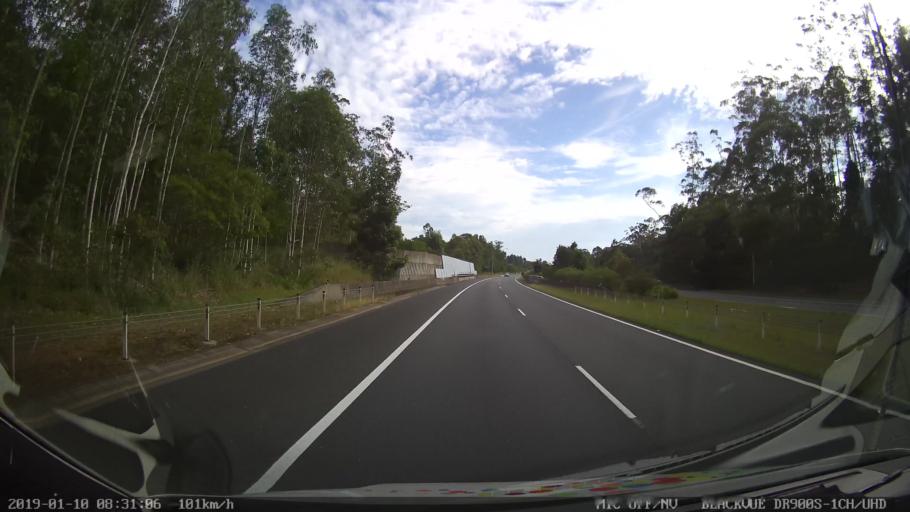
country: AU
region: New South Wales
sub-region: Coffs Harbour
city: Bonville
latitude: -30.3608
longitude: 153.0572
